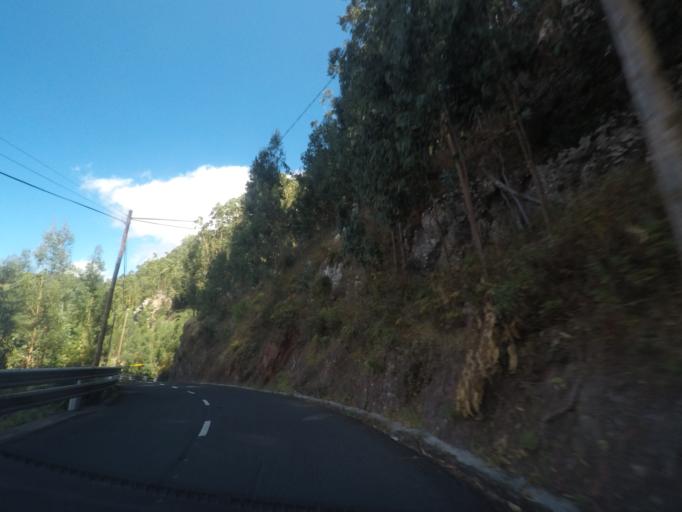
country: PT
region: Madeira
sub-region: Ribeira Brava
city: Campanario
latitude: 32.6870
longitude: -17.0320
